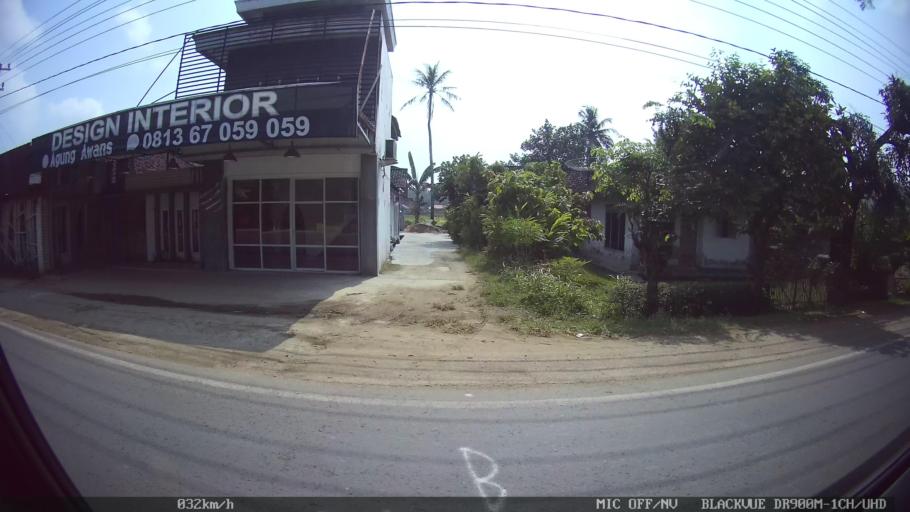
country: ID
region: Lampung
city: Gadingrejo
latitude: -5.3815
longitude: 105.0156
